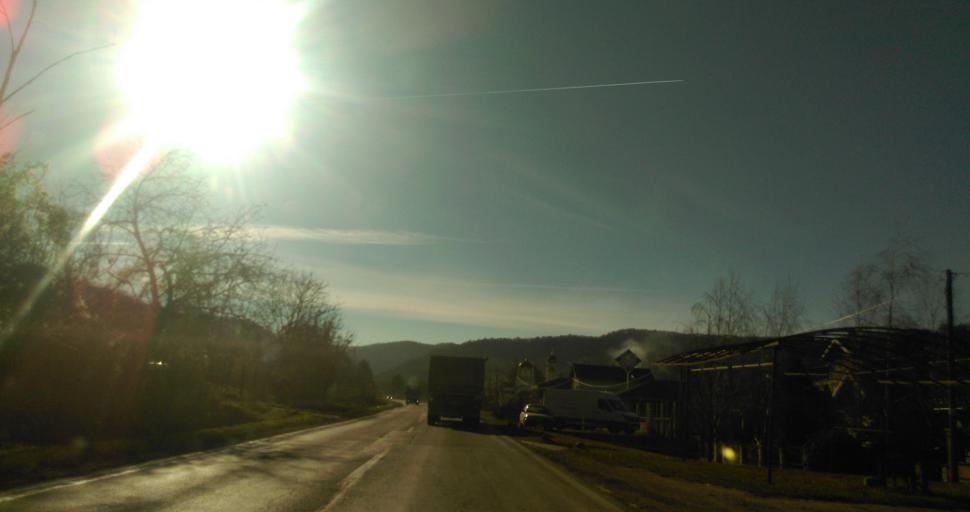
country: RS
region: Autonomna Pokrajina Vojvodina
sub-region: Juznobacki Okrug
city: Novi Sad
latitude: 45.1986
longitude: 19.8419
